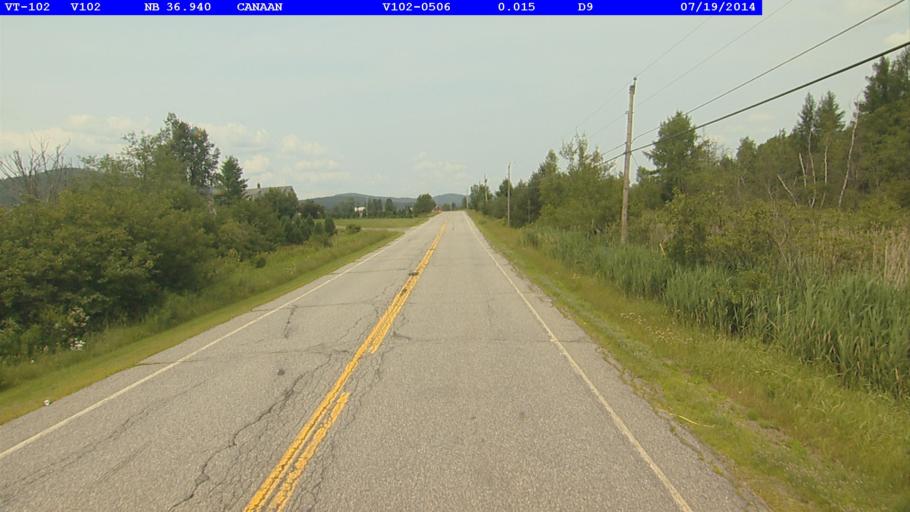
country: US
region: New Hampshire
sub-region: Coos County
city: Colebrook
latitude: 44.9111
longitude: -71.5069
